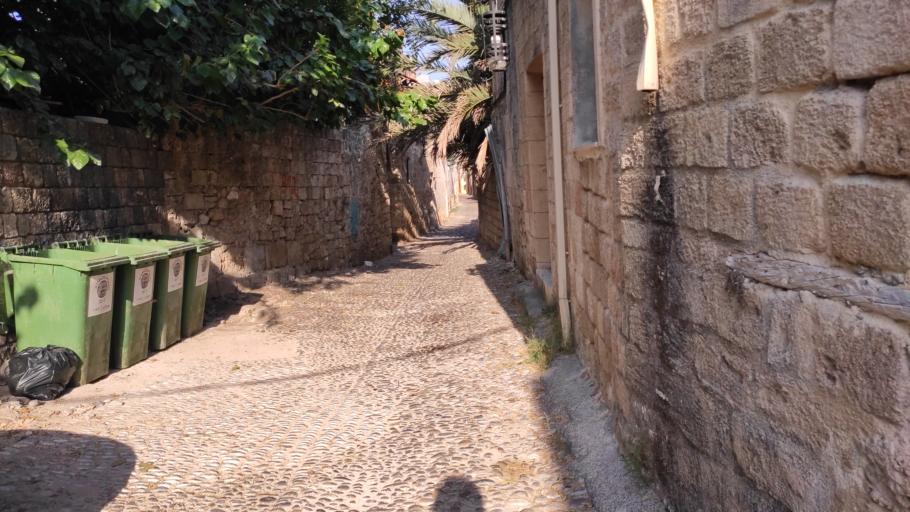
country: GR
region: South Aegean
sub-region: Nomos Dodekanisou
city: Rodos
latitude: 36.4413
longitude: 28.2269
